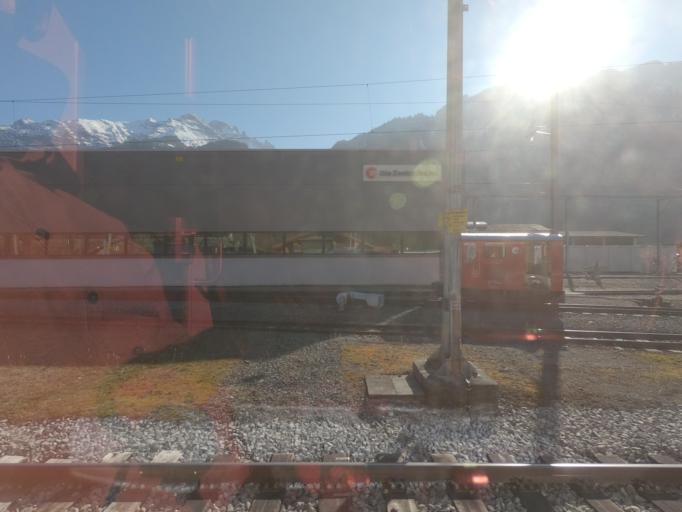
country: CH
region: Bern
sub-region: Interlaken-Oberhasli District
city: Meiringen
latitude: 46.7278
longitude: 8.1810
